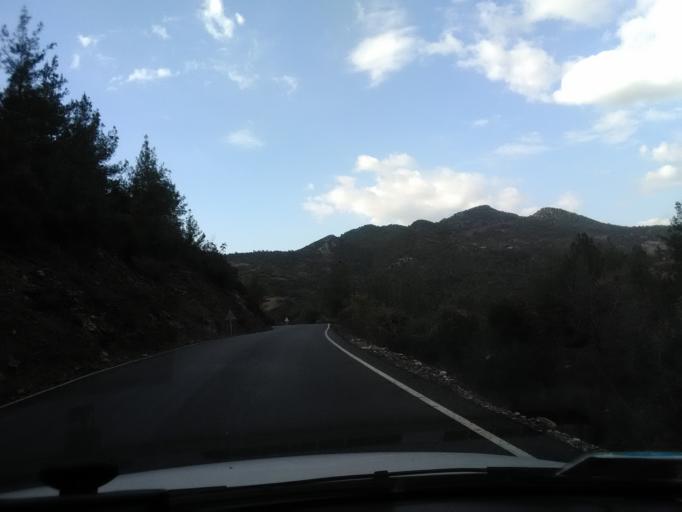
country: TR
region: Antalya
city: Gazipasa
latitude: 36.3013
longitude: 32.3830
